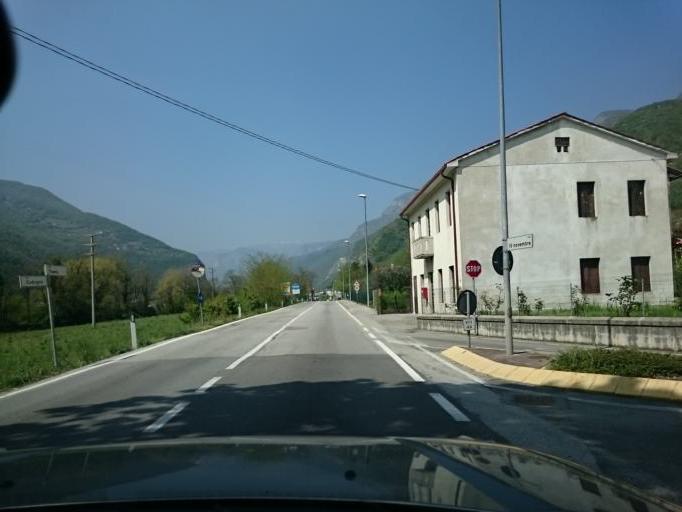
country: IT
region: Veneto
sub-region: Provincia di Vicenza
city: Solagna
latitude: 45.8199
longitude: 11.7137
